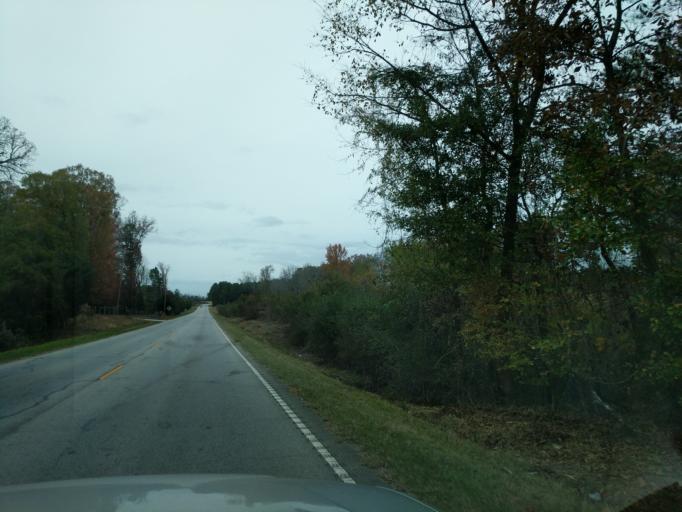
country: US
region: South Carolina
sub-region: Saluda County
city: Saluda
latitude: 34.0309
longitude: -81.7691
